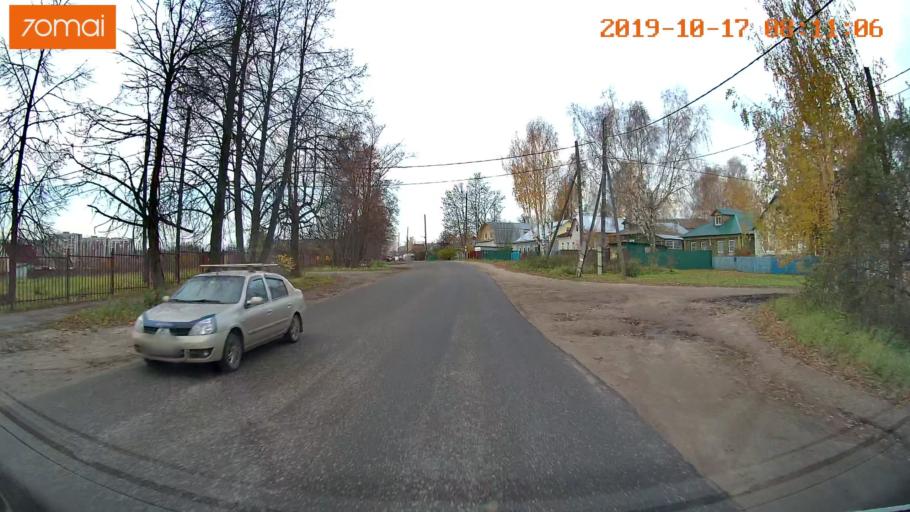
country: RU
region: Vladimir
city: Kol'chugino
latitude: 56.3042
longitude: 39.3744
